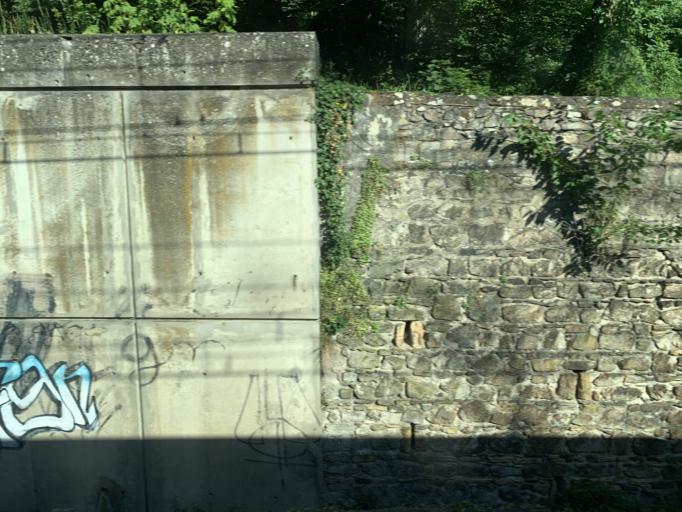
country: FR
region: Rhone-Alpes
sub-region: Departement du Rhone
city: Vernaison
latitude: 45.6364
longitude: 4.8075
